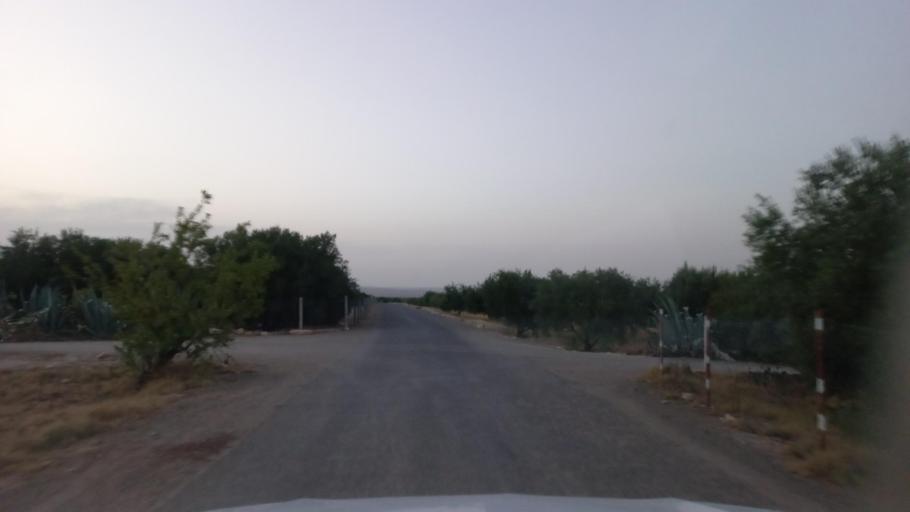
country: TN
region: Al Qasrayn
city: Kasserine
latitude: 35.2772
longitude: 9.0288
